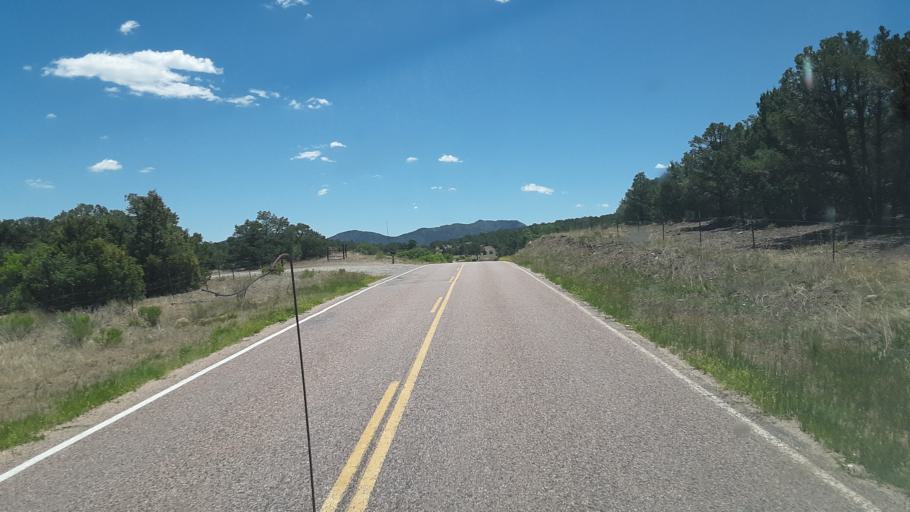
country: US
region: Colorado
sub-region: Custer County
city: Westcliffe
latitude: 38.3104
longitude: -105.6458
